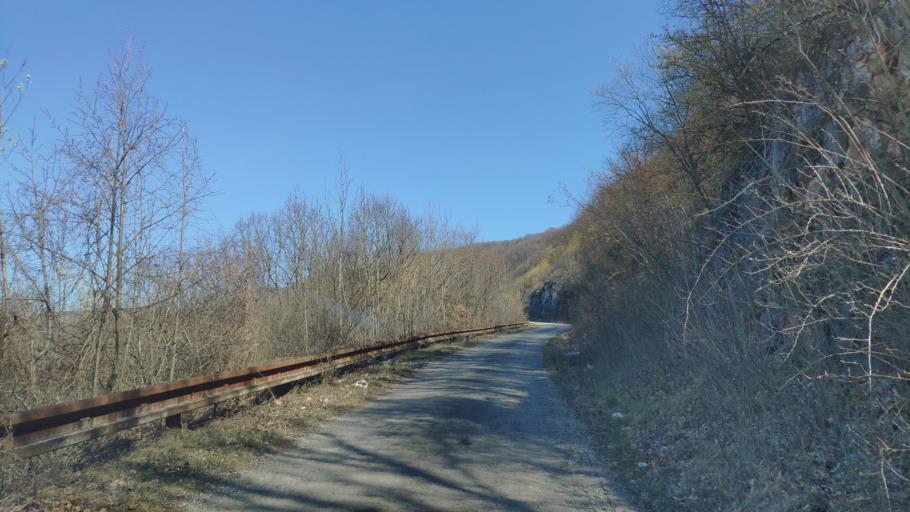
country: SK
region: Kosicky
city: Roznava
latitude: 48.5678
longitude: 20.4032
